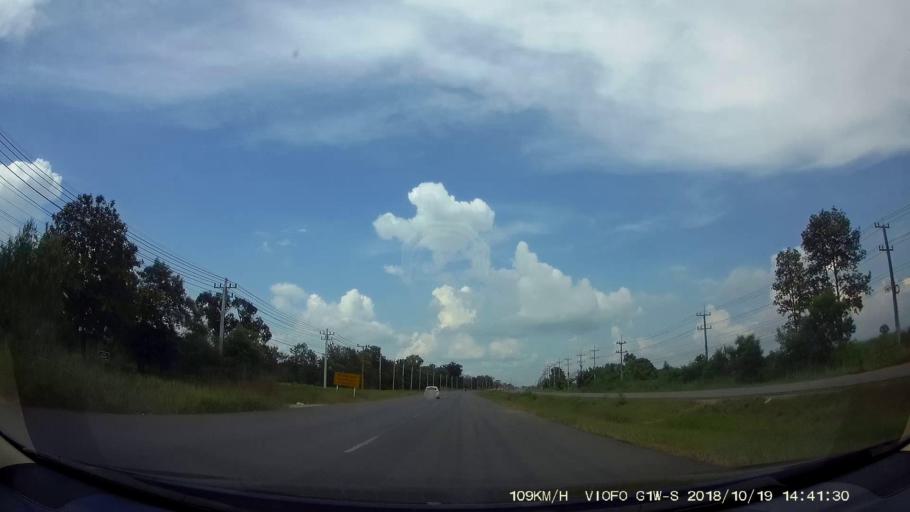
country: TH
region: Chaiyaphum
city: Phu Khiao
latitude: 16.2580
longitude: 102.1994
